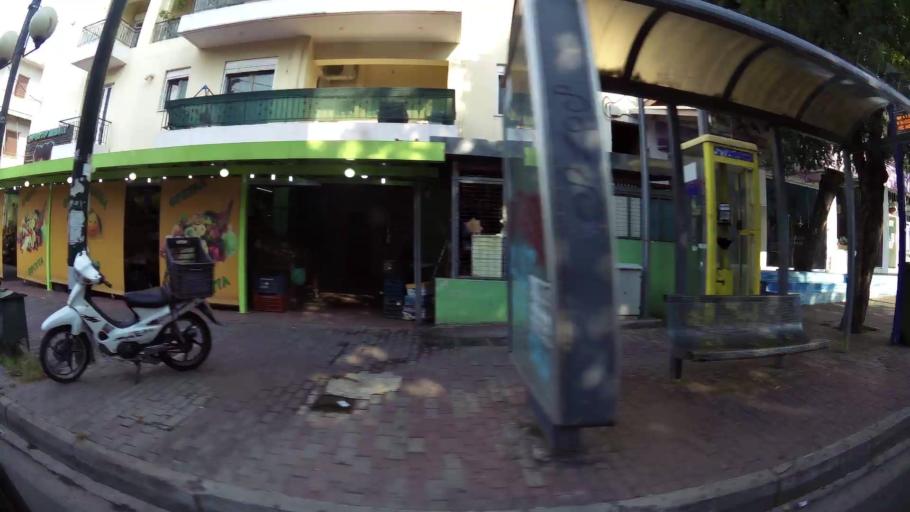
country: GR
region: Attica
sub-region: Nomarchia Athinas
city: Nea Filadelfeia
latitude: 38.0423
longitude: 23.7378
